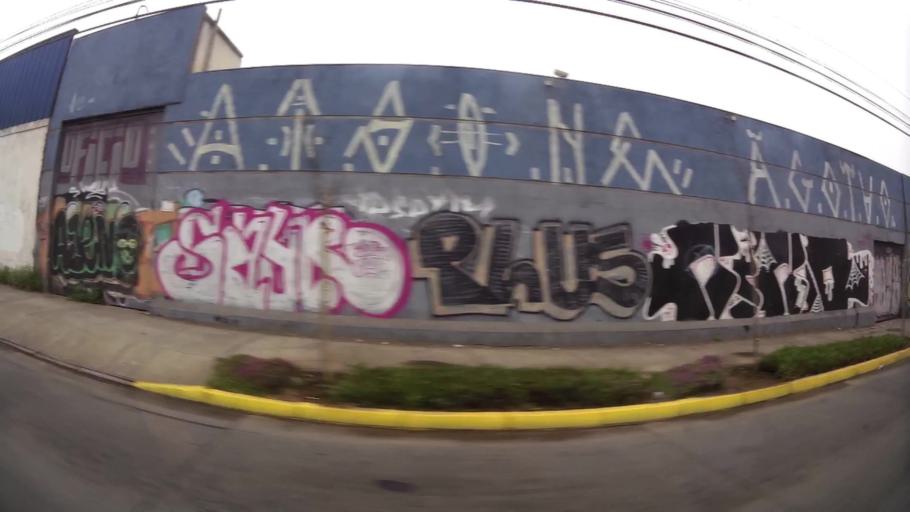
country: CL
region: Santiago Metropolitan
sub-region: Provincia de Santiago
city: Santiago
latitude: -33.4916
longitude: -70.6405
